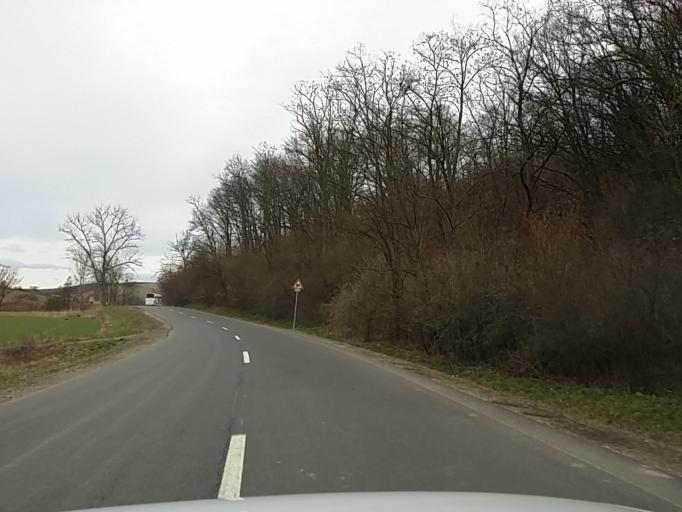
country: HU
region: Borsod-Abauj-Zemplen
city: Rudabanya
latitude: 48.4197
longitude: 20.5028
